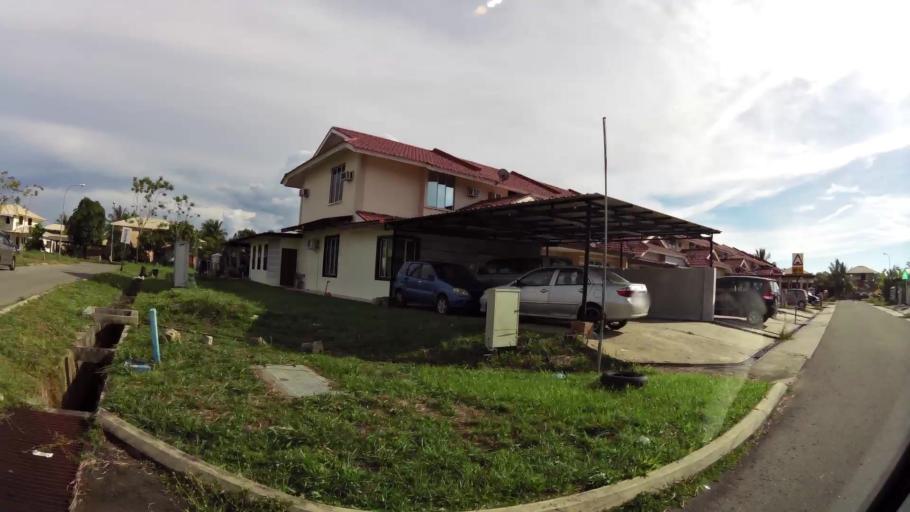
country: BN
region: Brunei and Muara
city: Bandar Seri Begawan
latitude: 4.9738
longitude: 115.0283
